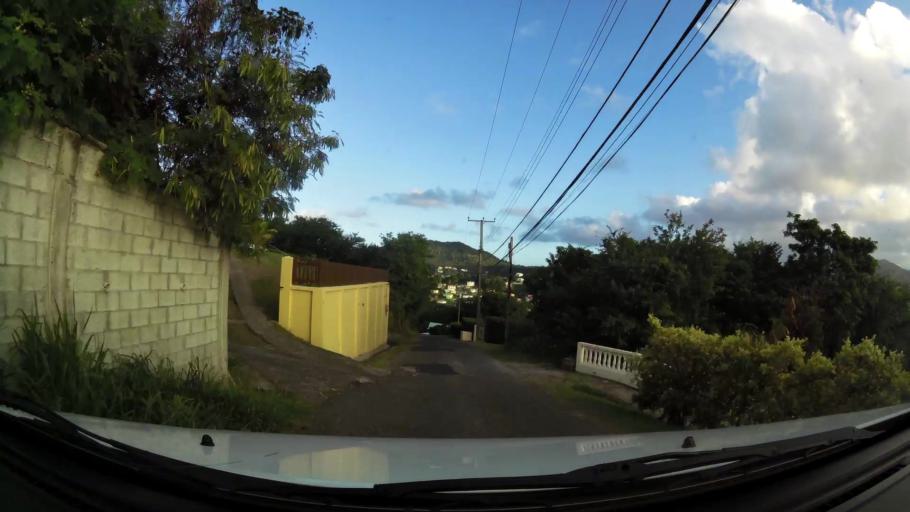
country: LC
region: Gros-Islet
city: Gros Islet
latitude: 14.0707
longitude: -60.9402
